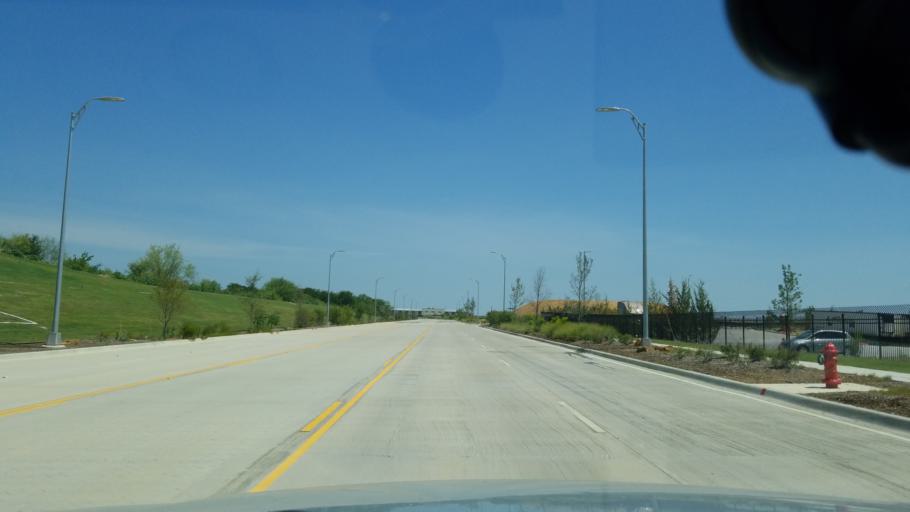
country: US
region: Texas
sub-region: Tarrant County
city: Euless
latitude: 32.8444
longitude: -97.0309
